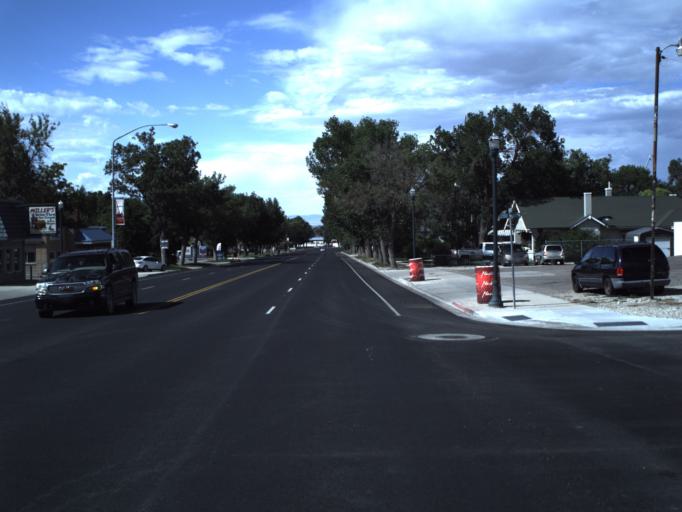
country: US
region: Utah
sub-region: Sanpete County
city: Manti
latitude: 39.2682
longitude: -111.6369
